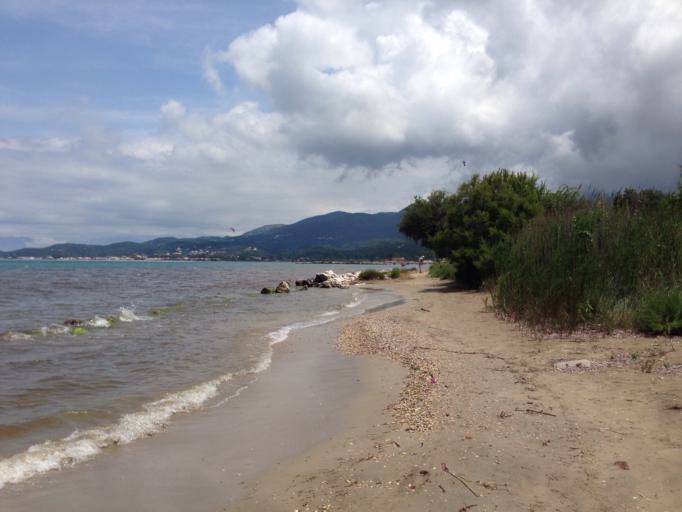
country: GR
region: Ionian Islands
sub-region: Nomos Kerkyras
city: Acharavi
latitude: 39.7937
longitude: 19.7839
